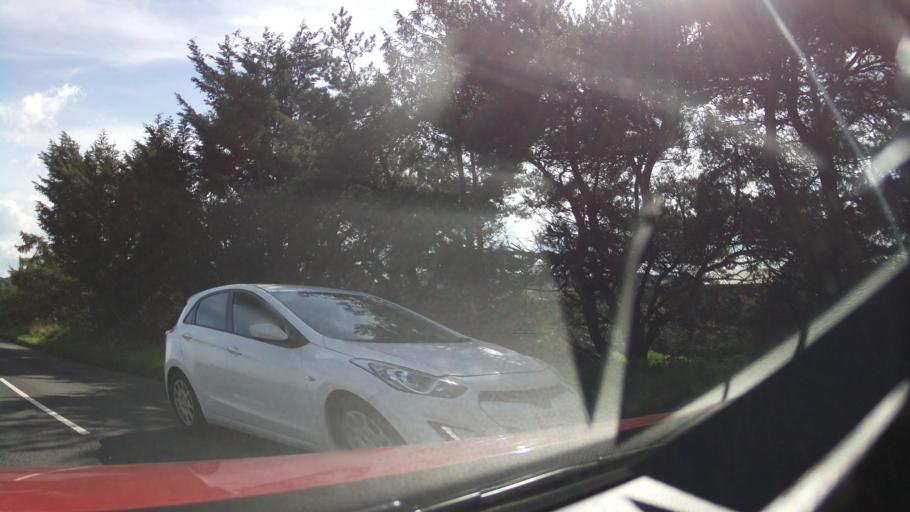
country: GB
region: Scotland
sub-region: Stirling
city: Bannockburn
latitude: 56.0798
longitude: -3.8963
